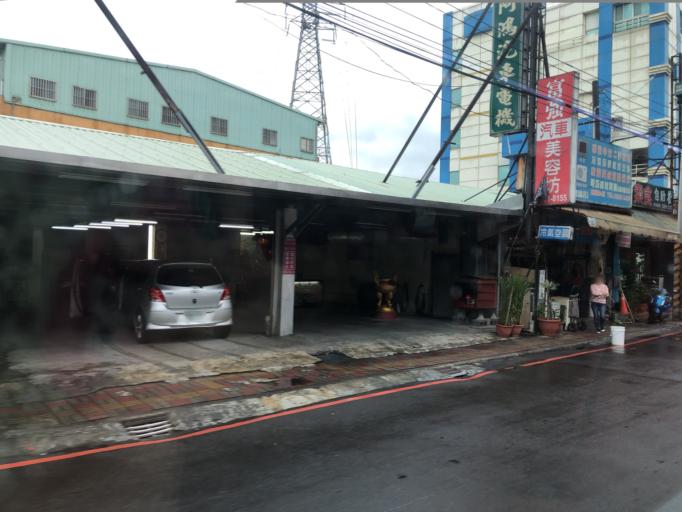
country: TW
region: Taipei
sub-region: Taipei
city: Banqiao
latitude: 25.0285
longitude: 121.4264
